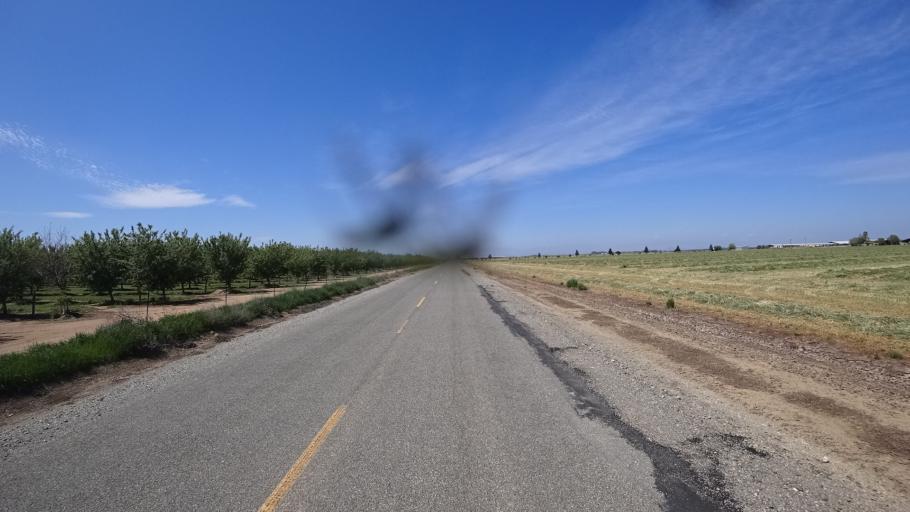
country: US
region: California
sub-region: Glenn County
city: Orland
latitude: 39.6527
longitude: -122.1460
